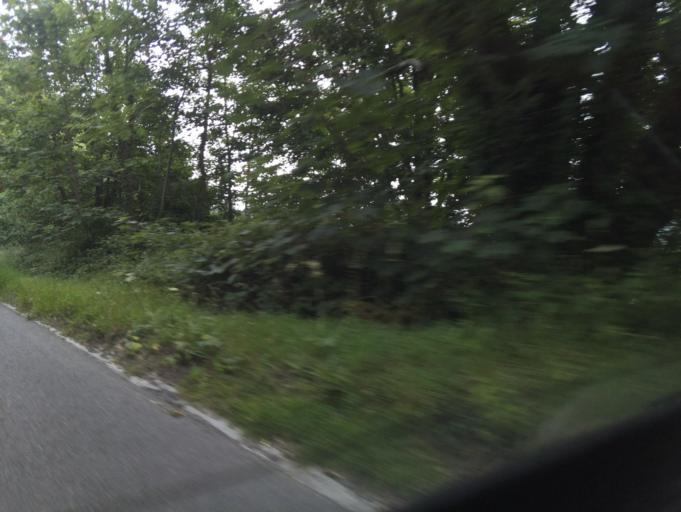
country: GB
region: England
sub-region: Dorset
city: Lyme Regis
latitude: 50.7375
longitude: -2.9329
